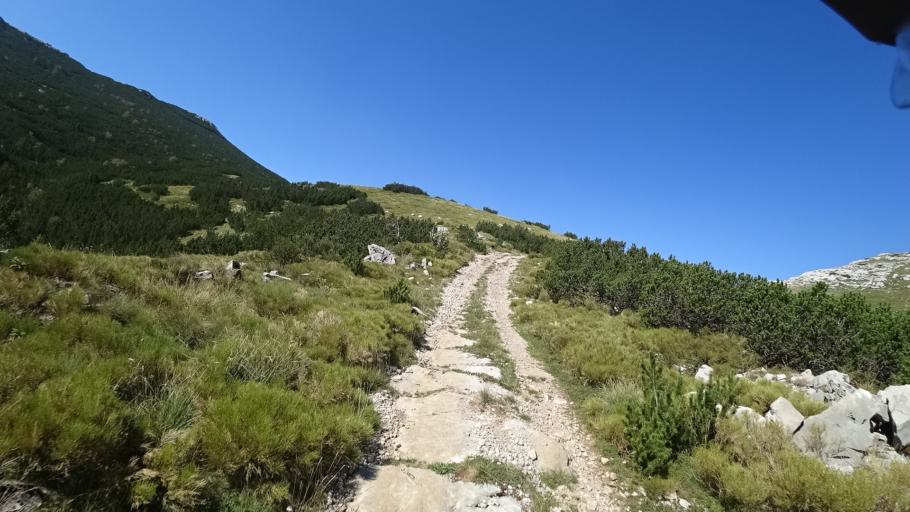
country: HR
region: Splitsko-Dalmatinska
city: Hrvace
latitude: 43.9386
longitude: 16.5876
